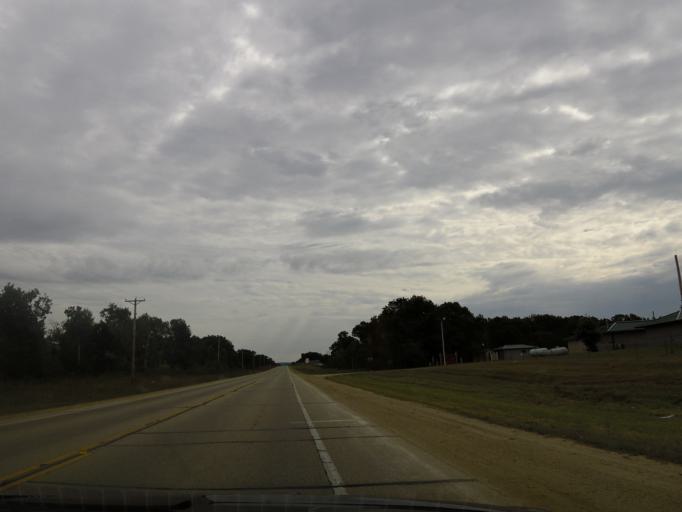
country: US
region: Wisconsin
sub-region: Monroe County
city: Sparta
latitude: 43.9425
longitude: -90.7533
